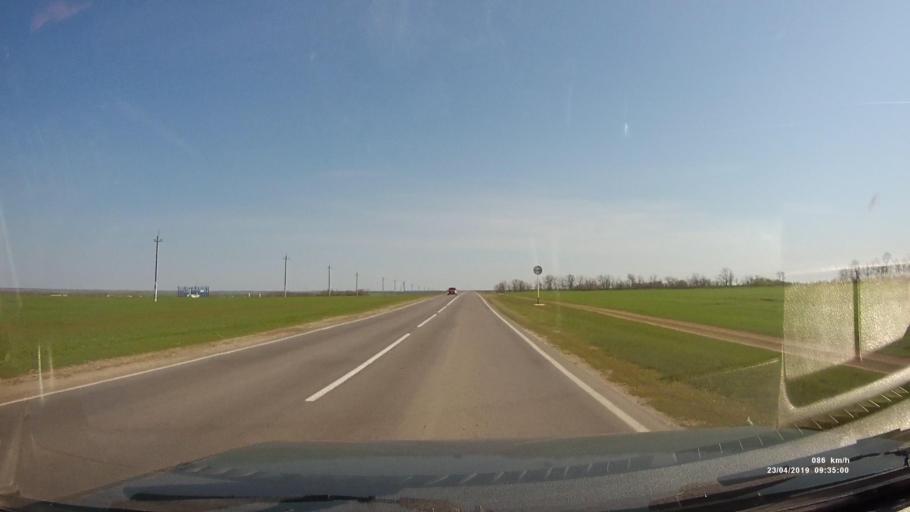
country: RU
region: Rostov
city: Gundorovskiy
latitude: 46.8172
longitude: 41.8646
